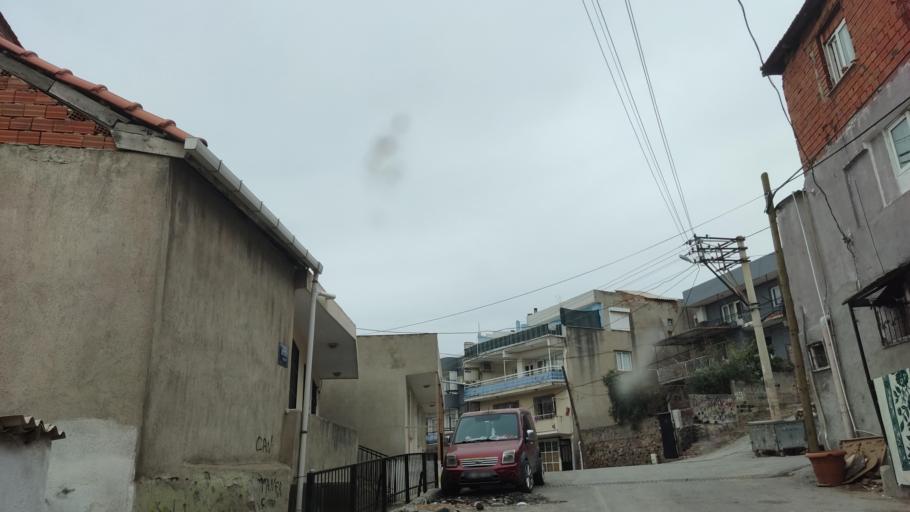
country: TR
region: Izmir
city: Karsiyaka
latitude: 38.4935
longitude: 27.0720
